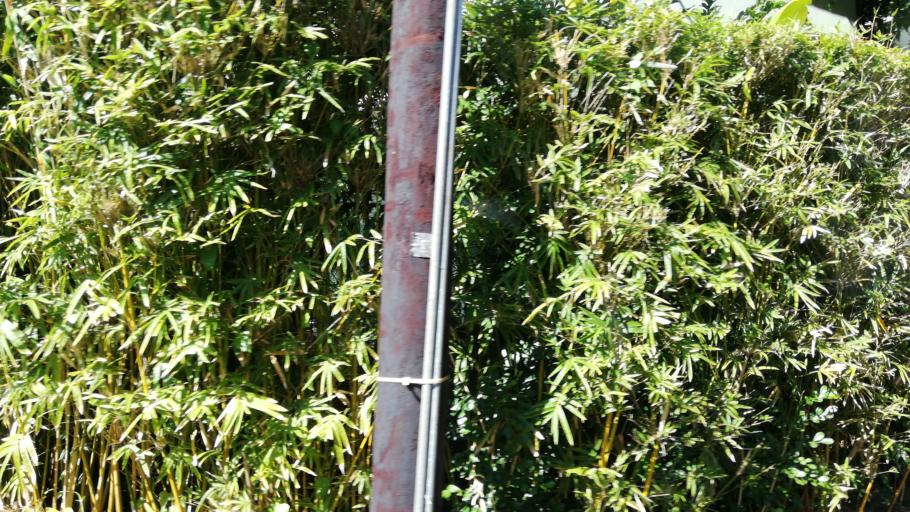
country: MU
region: Plaines Wilhems
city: Ebene
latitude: -20.2361
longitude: 57.4767
